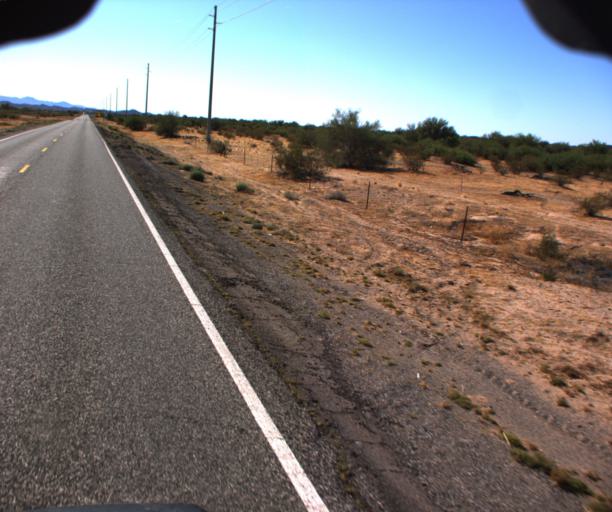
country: US
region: Arizona
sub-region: La Paz County
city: Cienega Springs
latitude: 33.9848
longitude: -114.0674
